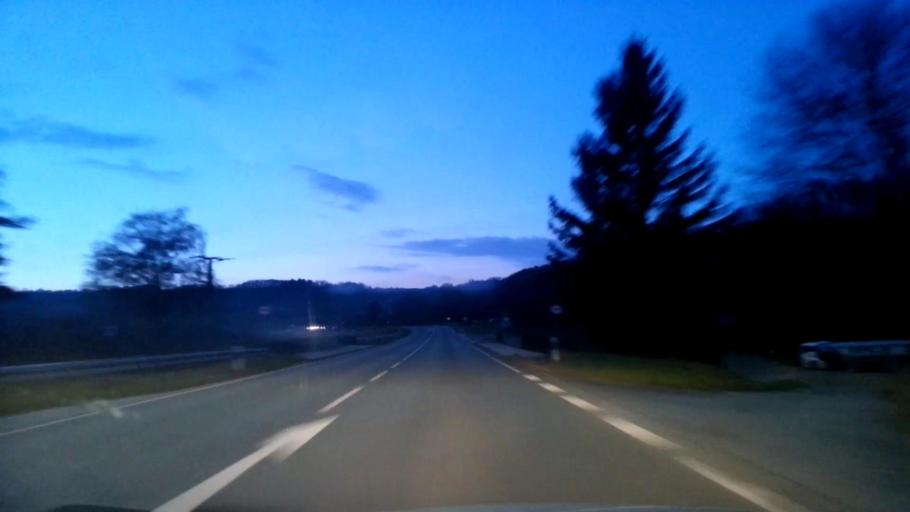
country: DE
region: Bavaria
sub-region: Upper Franconia
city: Reuth
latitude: 49.9709
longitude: 11.6868
